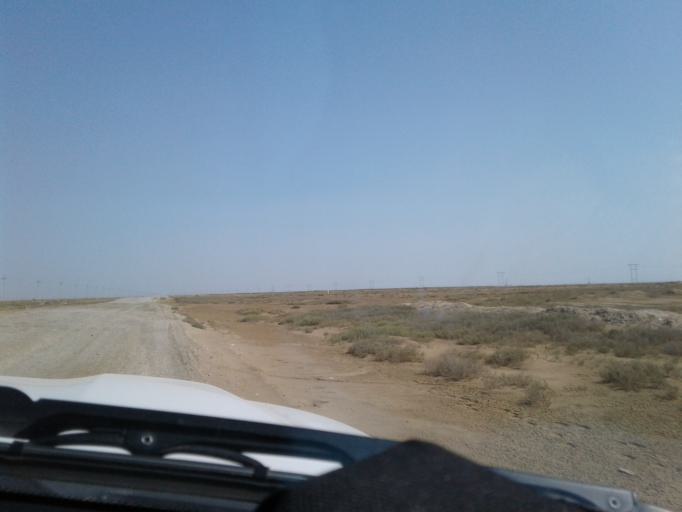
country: IR
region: Golestan
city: Gomishan
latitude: 37.7791
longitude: 53.9162
